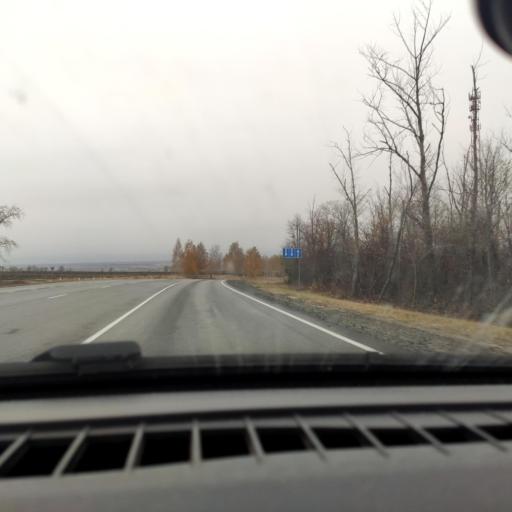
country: RU
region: Voronezj
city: Ostrogozhsk
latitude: 51.0186
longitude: 38.9827
